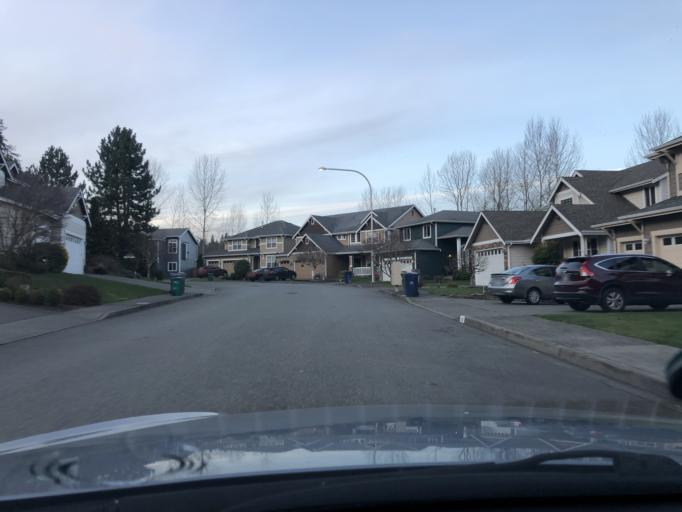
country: US
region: Washington
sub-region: King County
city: Auburn
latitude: 47.3178
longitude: -122.2517
